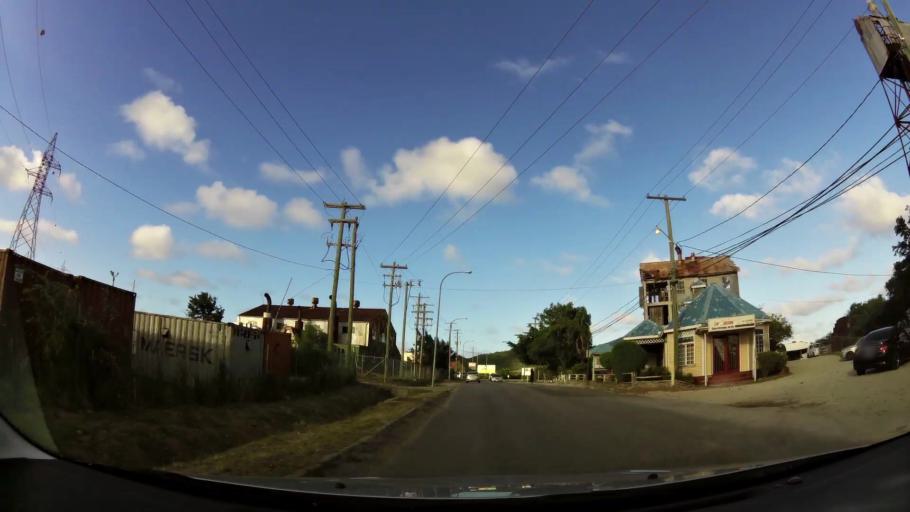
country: AG
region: Saint George
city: Piggotts
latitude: 17.1272
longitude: -61.8127
